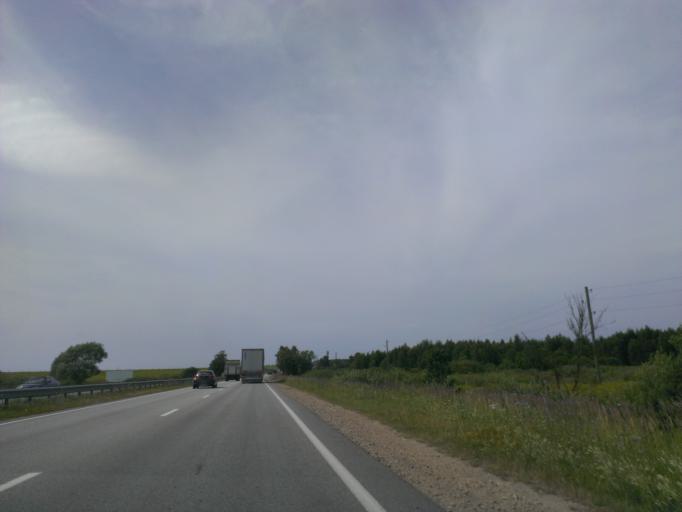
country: LV
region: Salaspils
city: Salaspils
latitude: 56.8463
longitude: 24.3713
